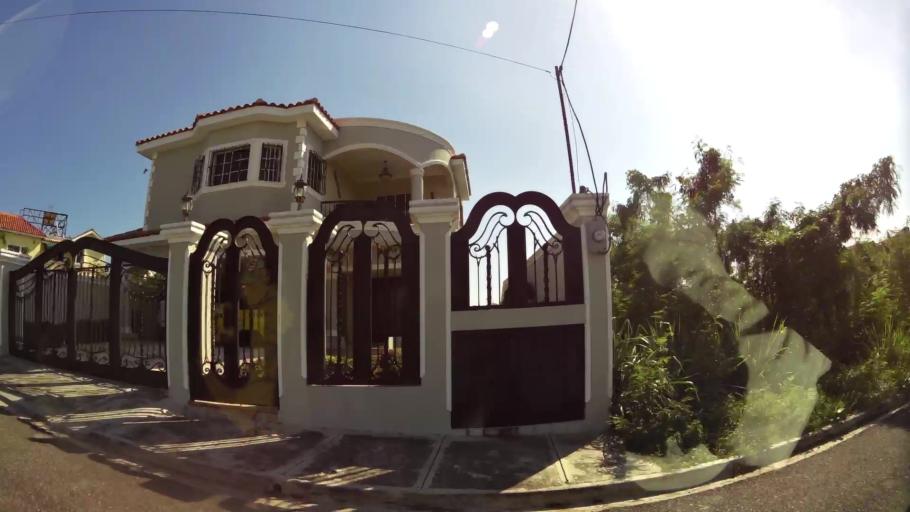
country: DO
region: Nacional
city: Santo Domingo
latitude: 18.4633
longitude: -69.9842
